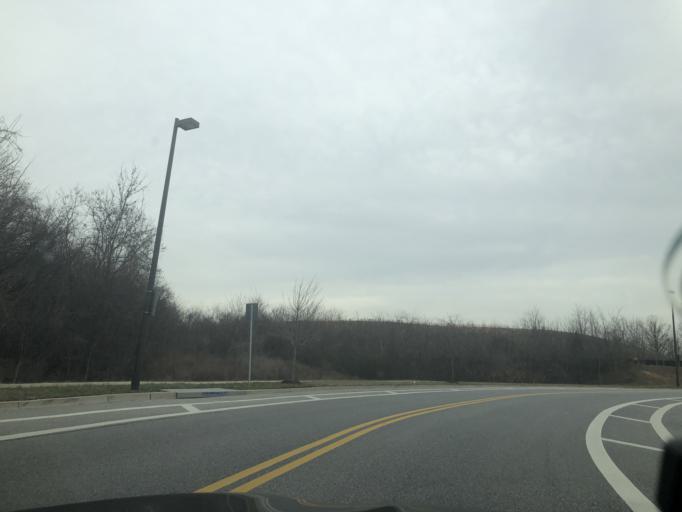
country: US
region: Maryland
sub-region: Prince George's County
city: Oxon Hill
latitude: 38.7996
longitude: -76.9945
